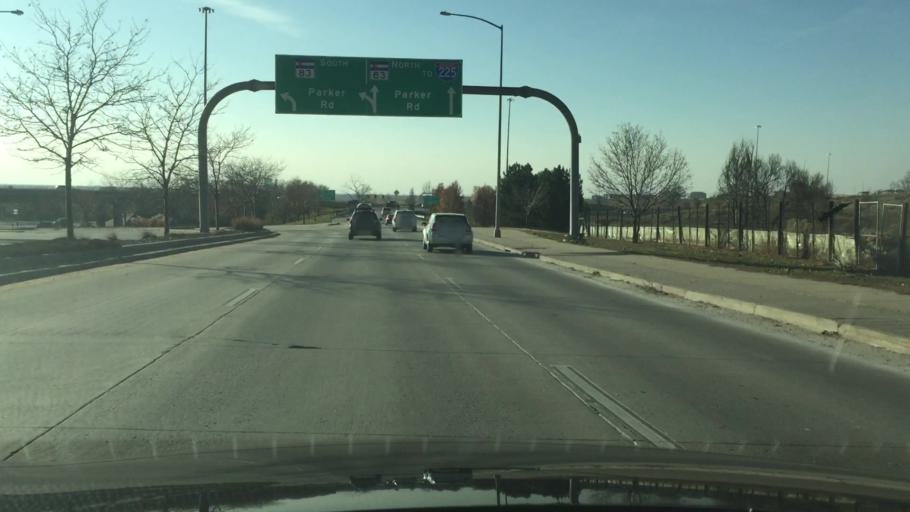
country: US
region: Colorado
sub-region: Arapahoe County
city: Dove Valley
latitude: 39.6532
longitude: -104.8289
